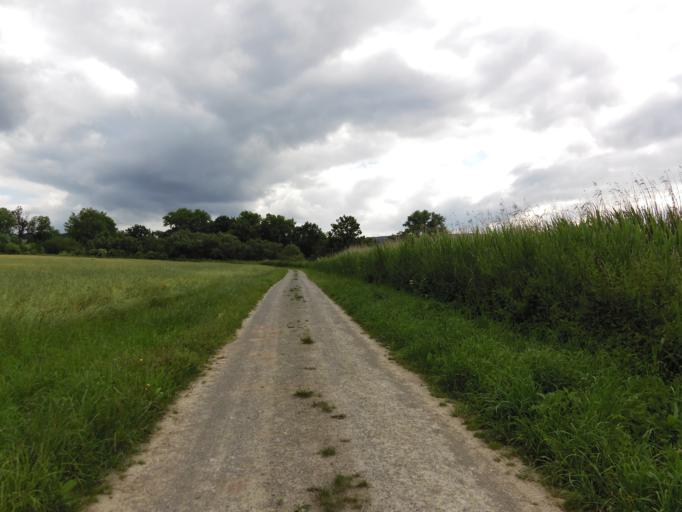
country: DE
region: Thuringia
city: Creuzburg
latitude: 51.0429
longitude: 10.2319
